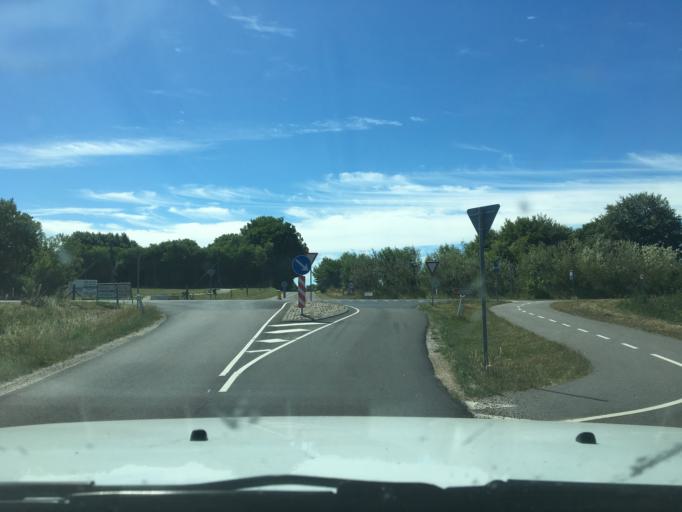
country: DK
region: Central Jutland
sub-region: Syddjurs Kommune
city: Ryomgard
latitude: 56.4303
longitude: 10.5674
